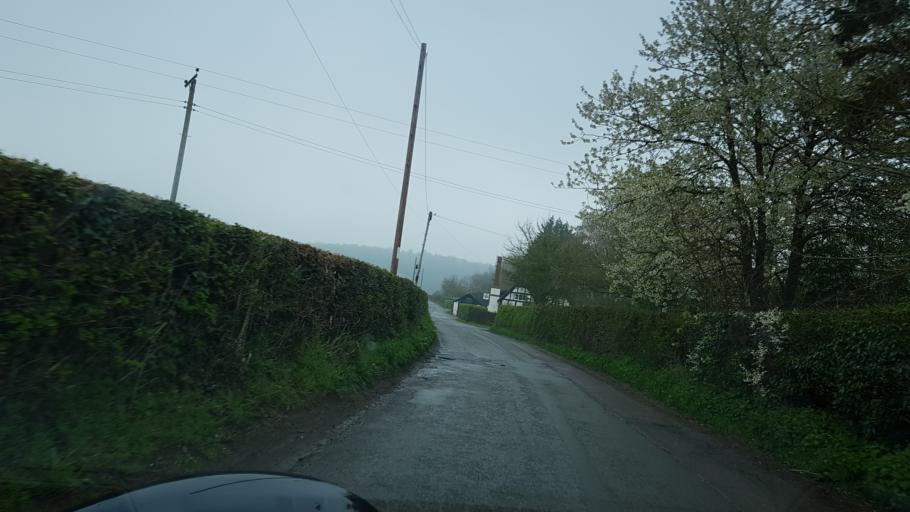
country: GB
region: England
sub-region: Herefordshire
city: Brockhampton
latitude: 52.0185
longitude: -2.5604
